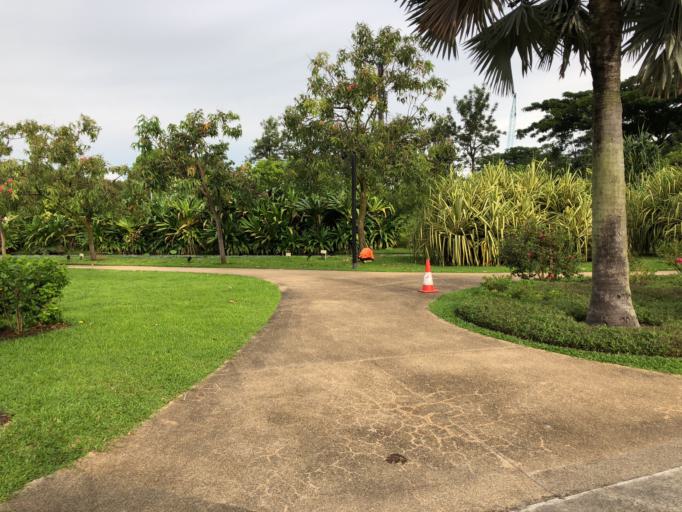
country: SG
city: Singapore
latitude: 1.2922
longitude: 103.8671
